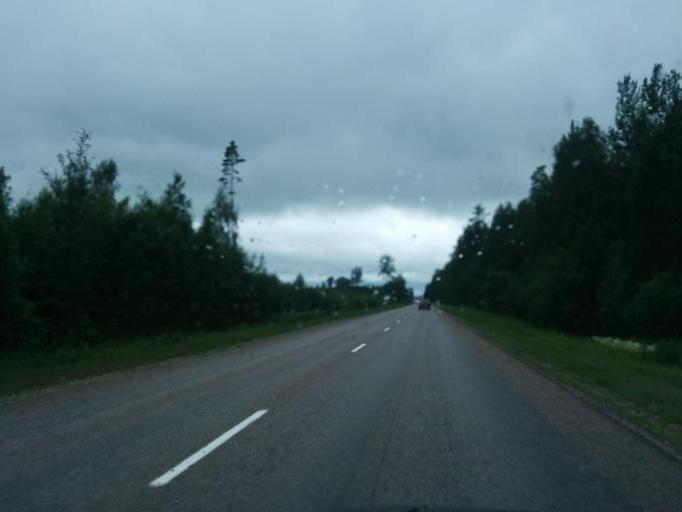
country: LV
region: Beverina
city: Murmuiza
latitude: 57.4876
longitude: 25.5881
